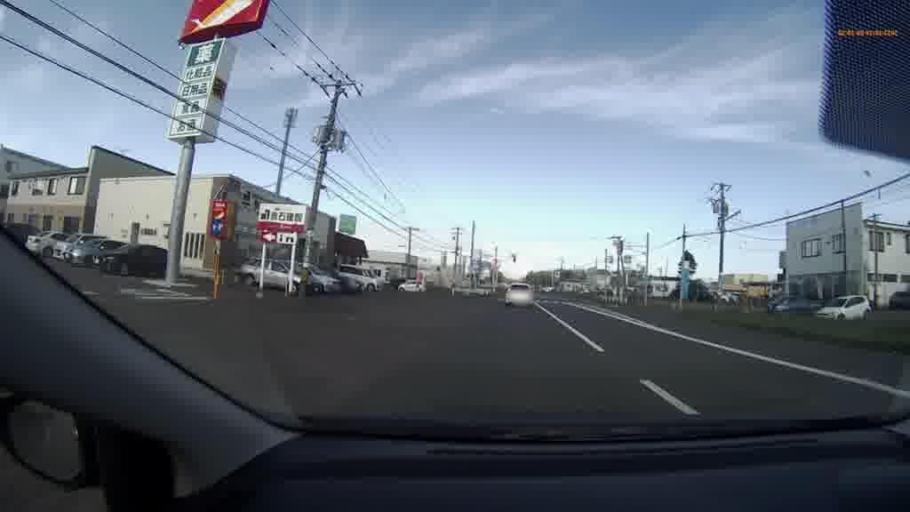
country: JP
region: Hokkaido
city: Kushiro
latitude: 43.0120
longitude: 144.4085
